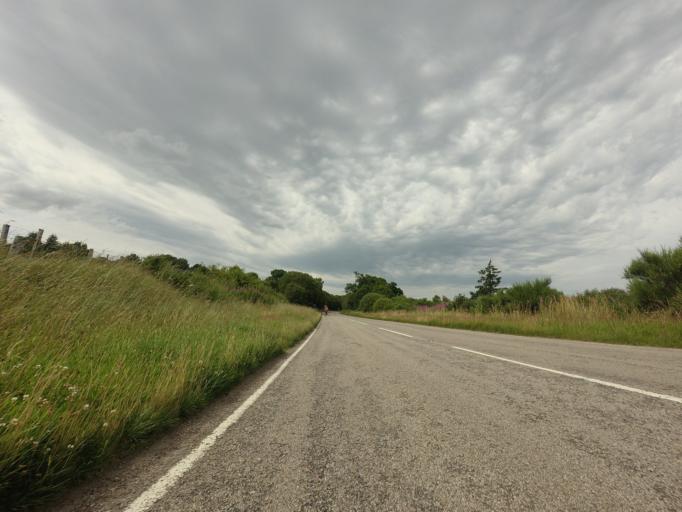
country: GB
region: Scotland
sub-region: Highland
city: Alness
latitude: 57.8746
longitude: -4.3549
